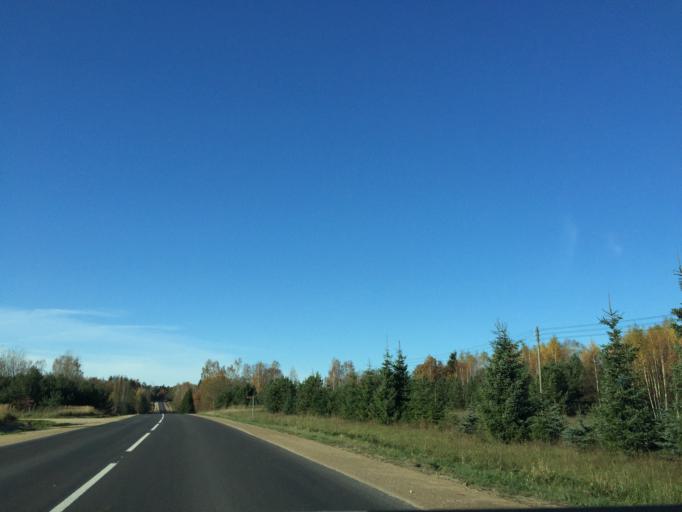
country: LV
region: Aizkraukles Rajons
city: Aizkraukle
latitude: 56.5904
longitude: 25.1853
